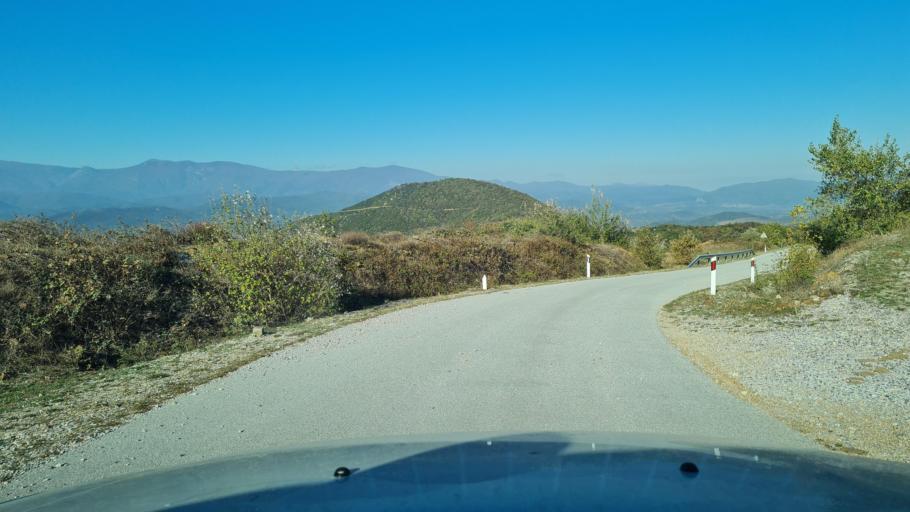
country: MK
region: Bogdanci
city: Bogdanci
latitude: 41.2234
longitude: 22.5562
